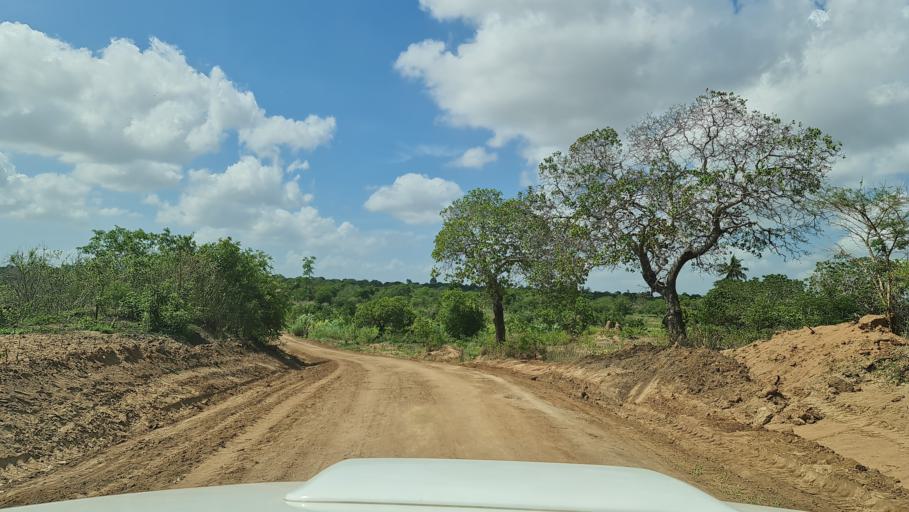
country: MZ
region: Nampula
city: Ilha de Mocambique
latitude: -15.0112
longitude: 40.5604
